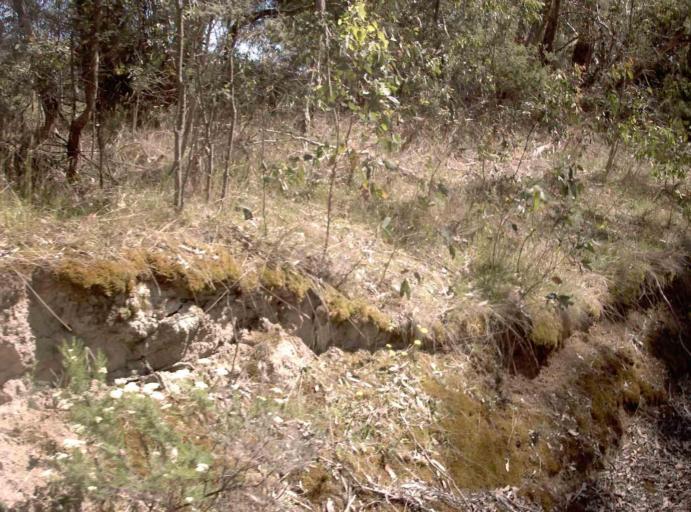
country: AU
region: New South Wales
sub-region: Bombala
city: Bombala
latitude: -37.0570
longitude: 148.8042
